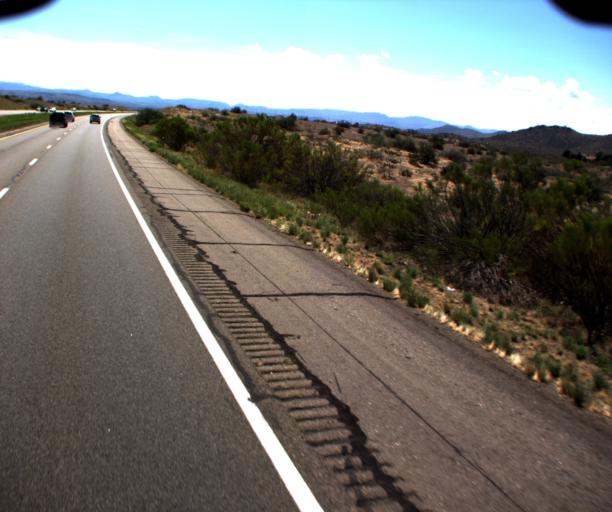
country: US
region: Arizona
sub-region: Yavapai County
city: Spring Valley
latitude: 34.3482
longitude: -112.1501
